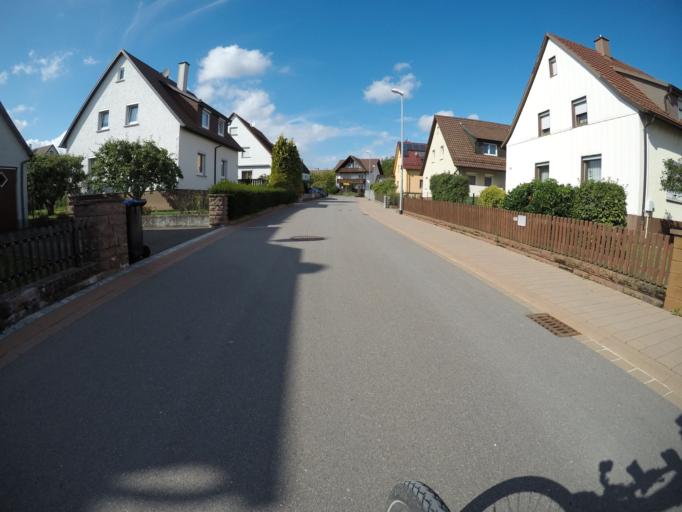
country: DE
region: Baden-Wuerttemberg
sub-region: Regierungsbezirk Stuttgart
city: Gartringen
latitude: 48.6438
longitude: 8.9060
